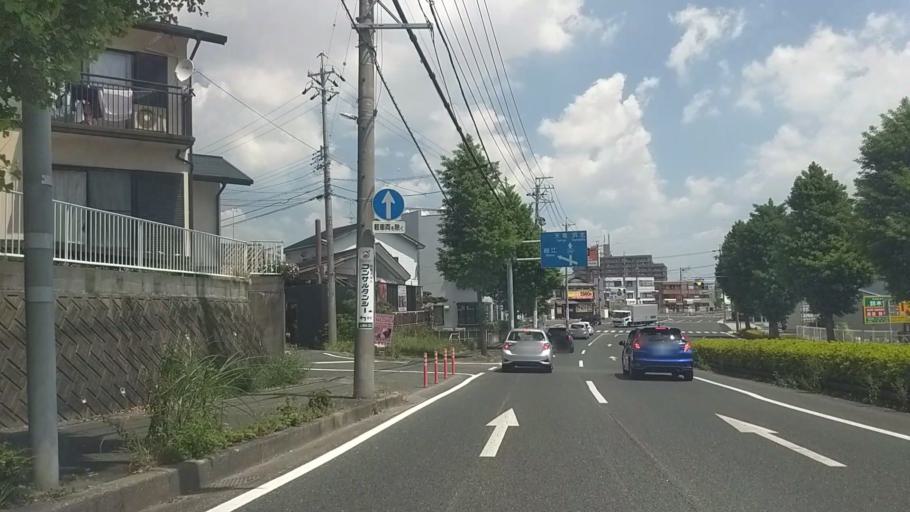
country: JP
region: Shizuoka
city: Hamamatsu
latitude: 34.7436
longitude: 137.7402
